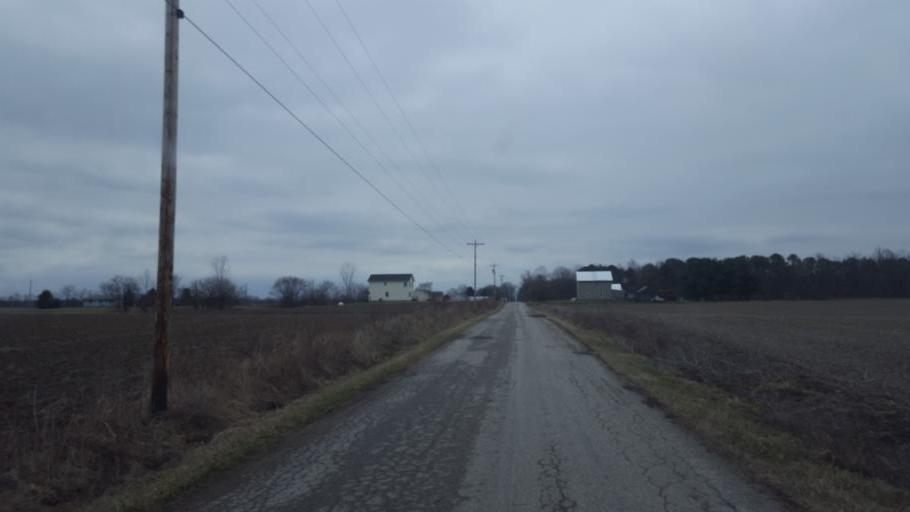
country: US
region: Ohio
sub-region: Delaware County
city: Ashley
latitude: 40.4332
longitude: -83.0058
